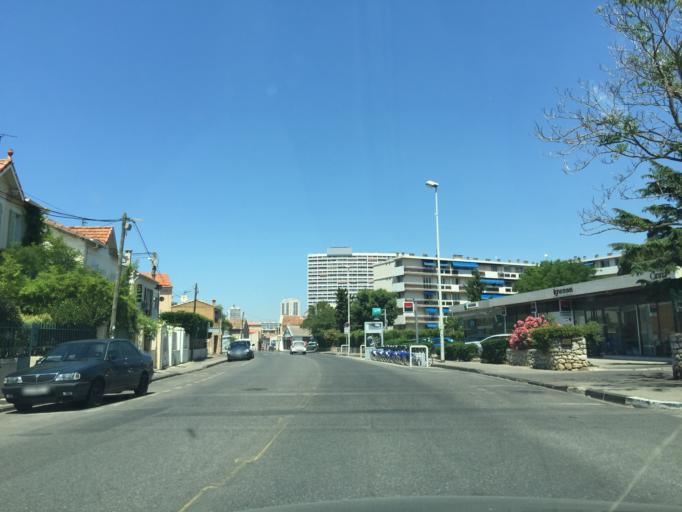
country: FR
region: Provence-Alpes-Cote d'Azur
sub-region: Departement des Bouches-du-Rhone
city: Marseille 09
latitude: 43.2602
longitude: 5.3940
